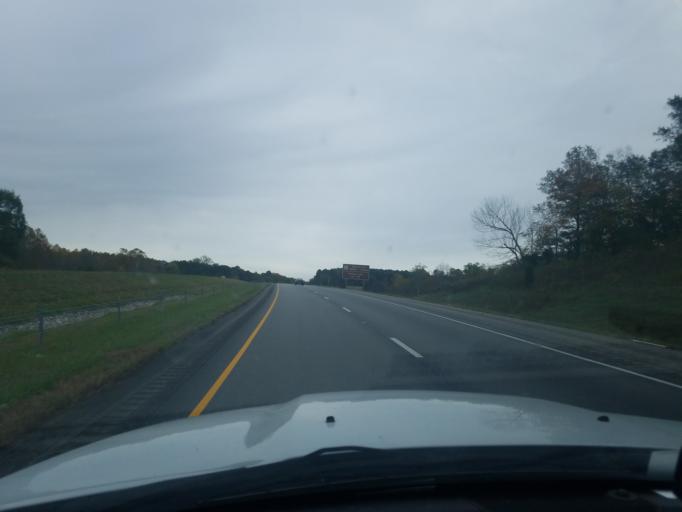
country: US
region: Indiana
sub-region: Crawford County
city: English
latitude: 38.2295
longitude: -86.6131
